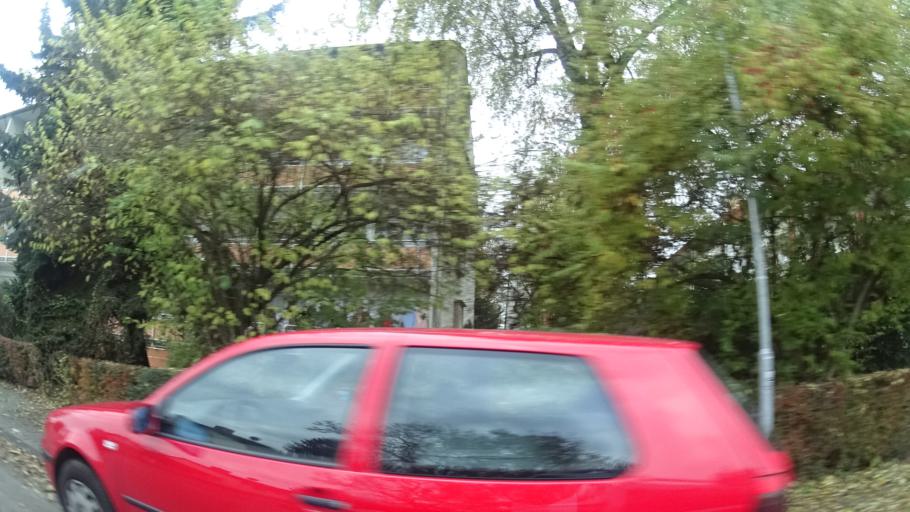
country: DE
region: Baden-Wuerttemberg
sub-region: Karlsruhe Region
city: Weinheim
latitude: 49.5431
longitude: 8.6422
